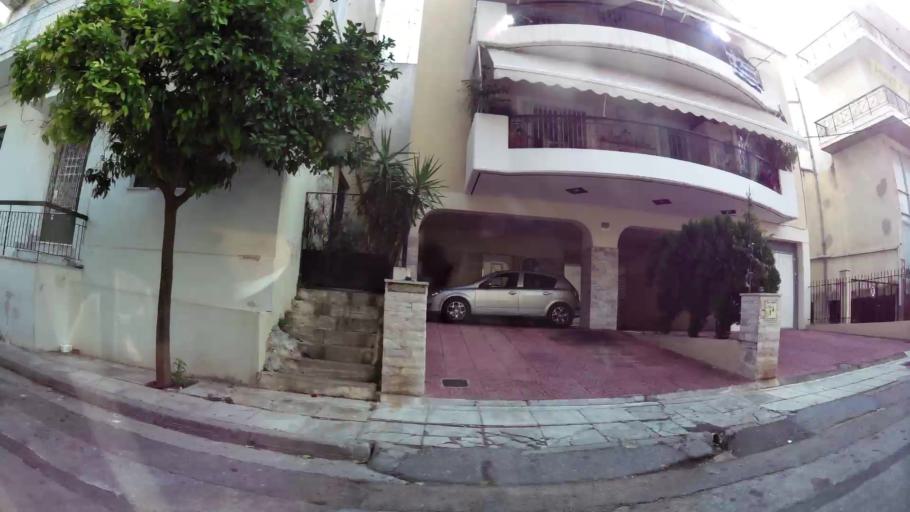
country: GR
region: Attica
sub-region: Nomarchia Athinas
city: Galatsi
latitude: 38.0145
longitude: 23.7578
